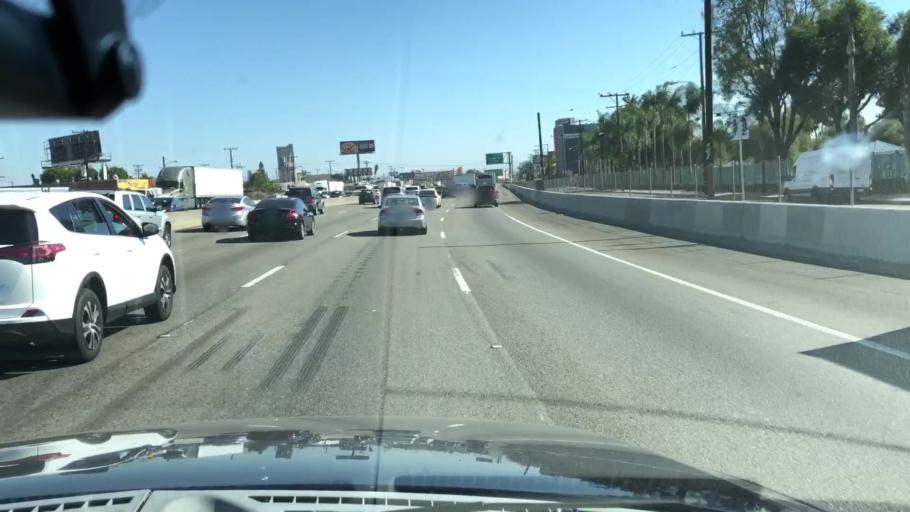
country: US
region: California
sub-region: Los Angeles County
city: East Los Angeles
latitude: 34.0146
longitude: -118.1688
